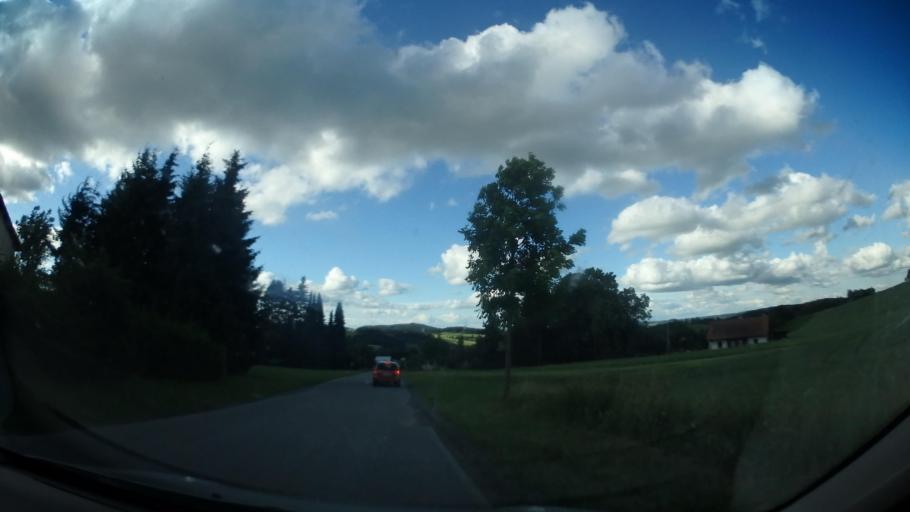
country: CZ
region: Vysocina
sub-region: Okres Zd'ar nad Sazavou
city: Jimramov
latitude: 49.6023
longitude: 16.1876
